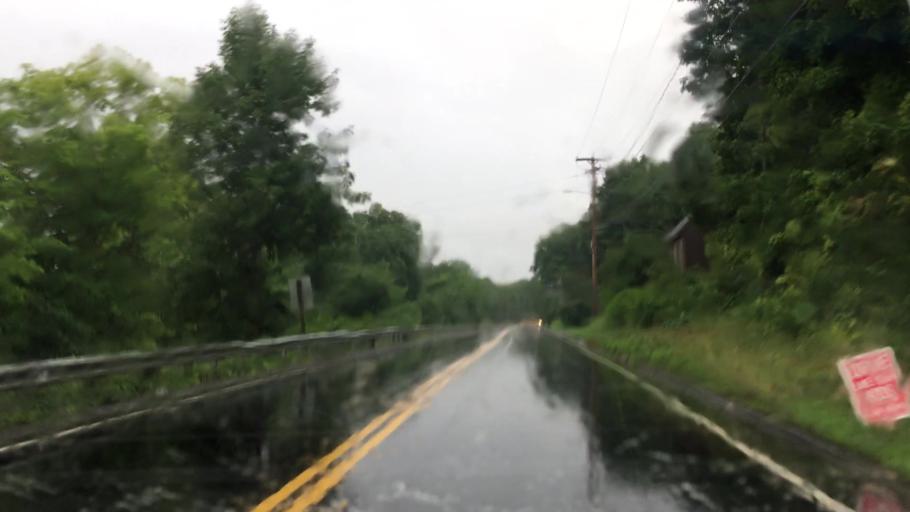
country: US
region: Maine
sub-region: Kennebec County
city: Pittston
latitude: 44.2216
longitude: -69.7646
